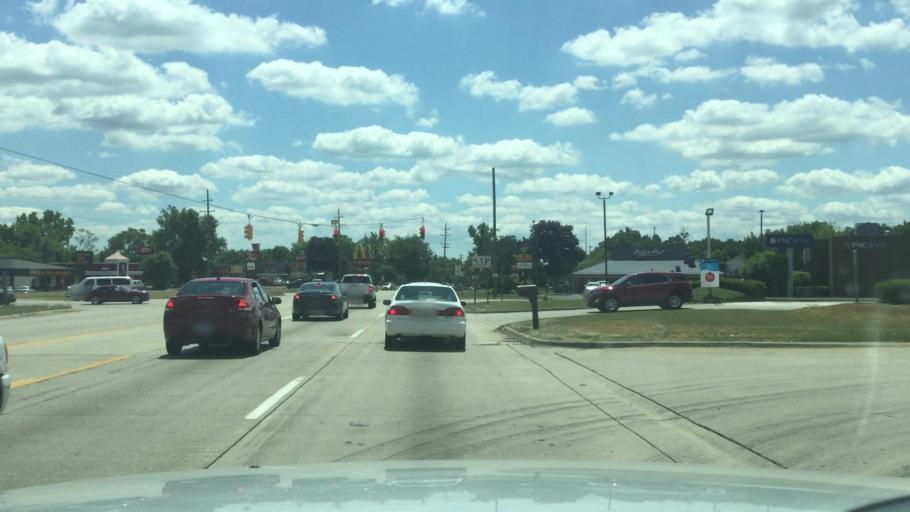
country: US
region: Michigan
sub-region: Wayne County
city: Belleville
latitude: 42.2160
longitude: -83.5446
